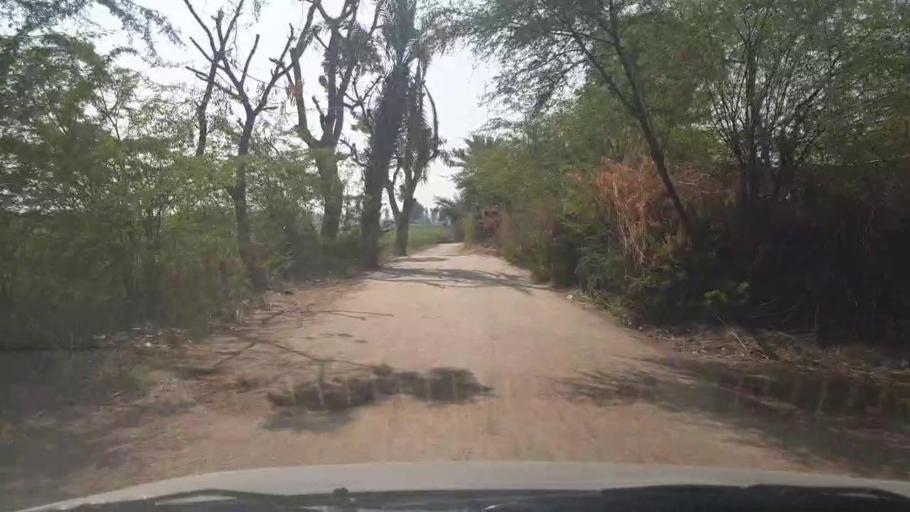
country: PK
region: Sindh
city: Mirwah Gorchani
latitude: 25.2787
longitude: 69.1489
